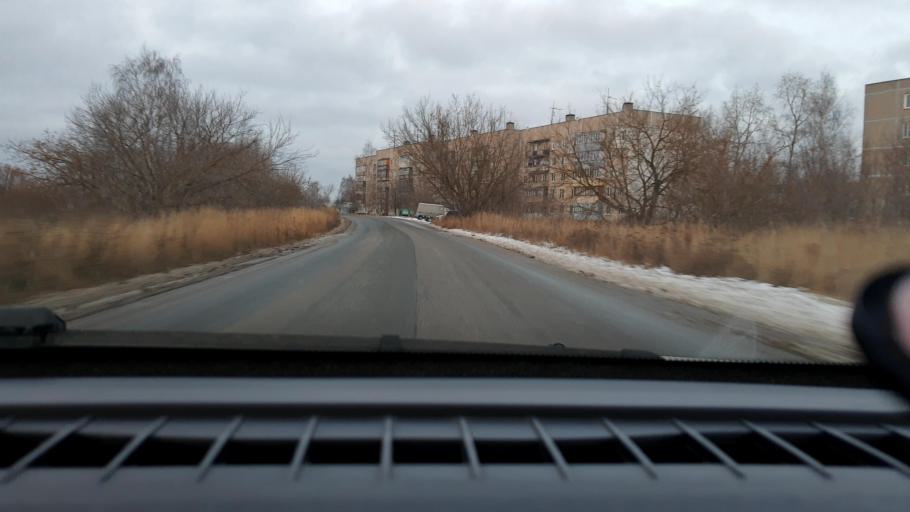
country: RU
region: Nizjnij Novgorod
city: Gorbatovka
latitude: 56.2429
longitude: 43.7451
